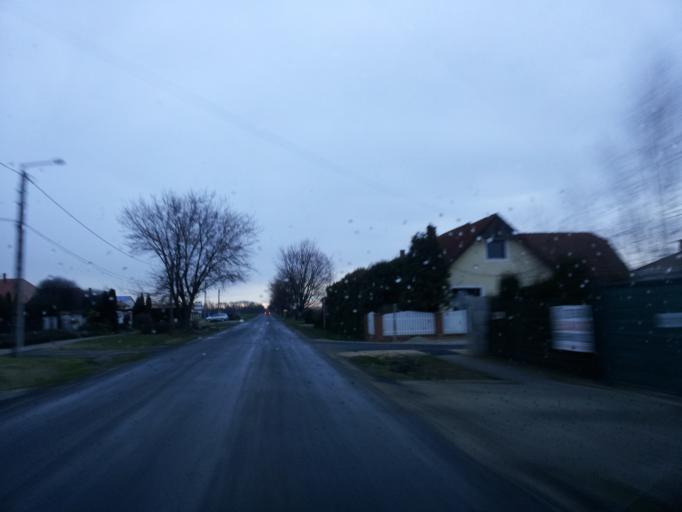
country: AT
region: Burgenland
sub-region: Politischer Bezirk Oberpullendorf
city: Nikitsch
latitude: 47.4877
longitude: 16.7375
